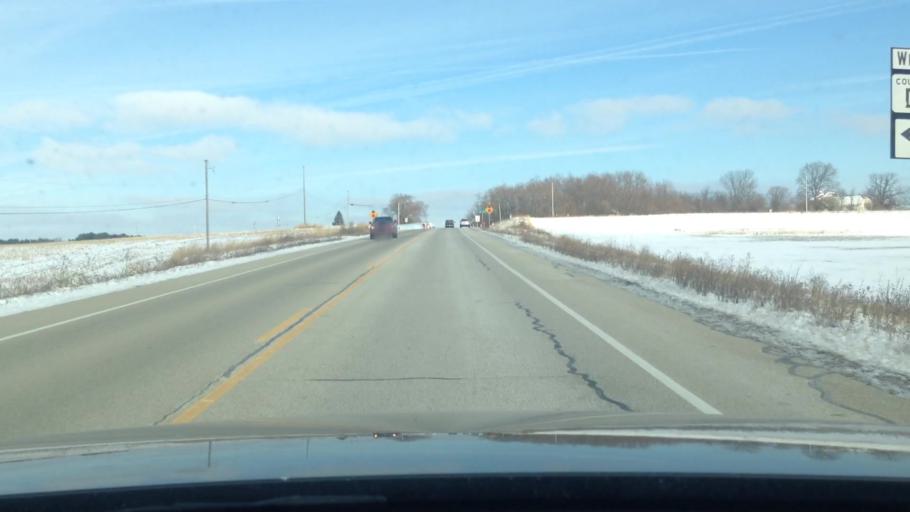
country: US
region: Wisconsin
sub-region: Walworth County
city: East Troy
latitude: 42.7431
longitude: -88.4061
